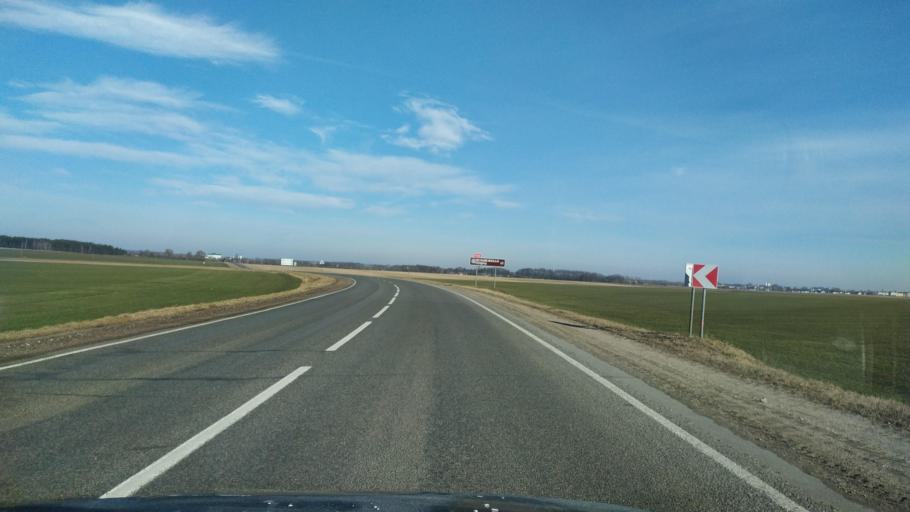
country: BY
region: Brest
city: Kamyanyets
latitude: 52.3714
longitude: 23.7924
